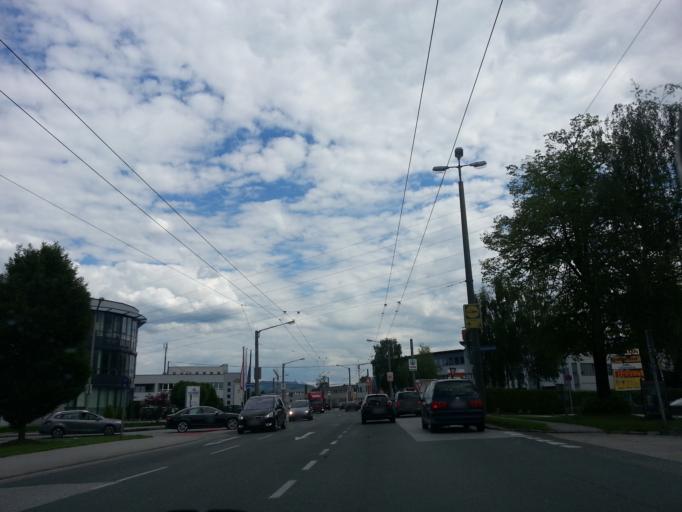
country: DE
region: Bavaria
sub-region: Upper Bavaria
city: Freilassing
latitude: 47.8306
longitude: 13.0020
